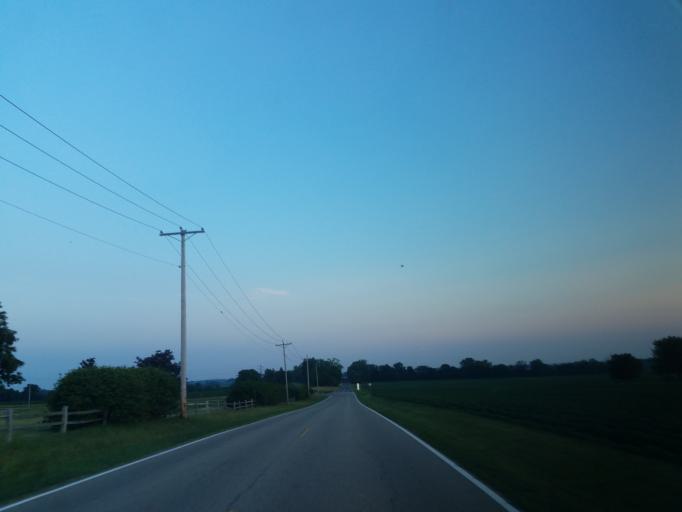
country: US
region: Illinois
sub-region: McLean County
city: Bloomington
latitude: 40.4431
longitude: -89.0055
